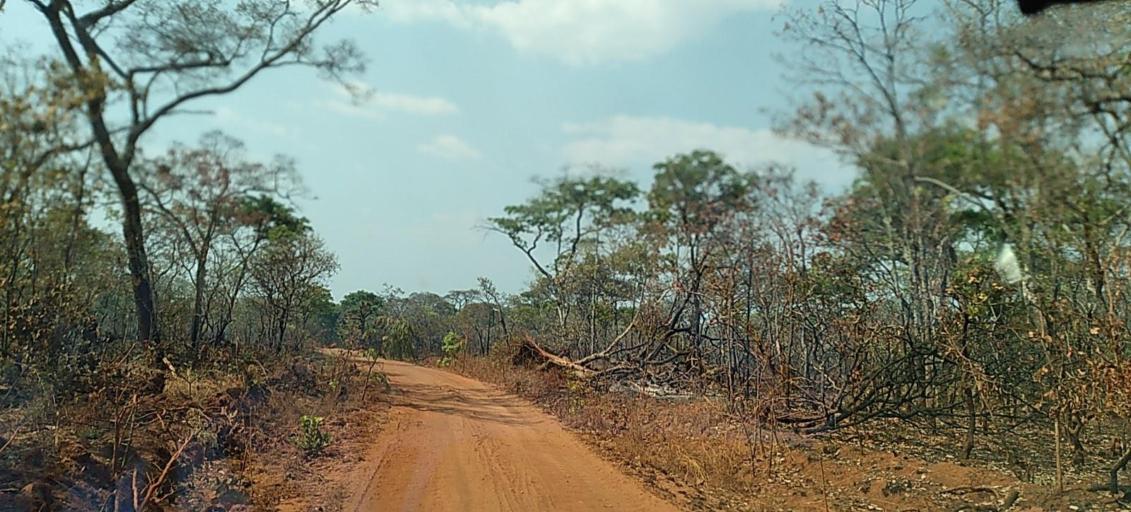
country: ZM
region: North-Western
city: Kasempa
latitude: -13.3147
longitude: 26.0584
